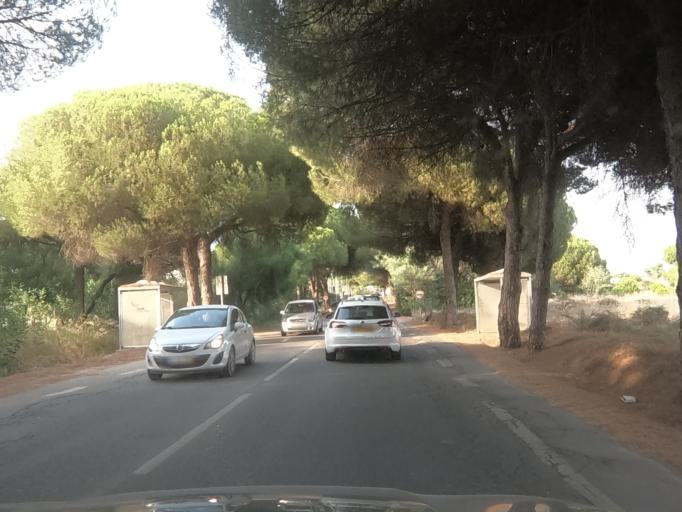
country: PT
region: Faro
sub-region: Loule
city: Quarteira
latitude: 37.0824
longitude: -8.0851
